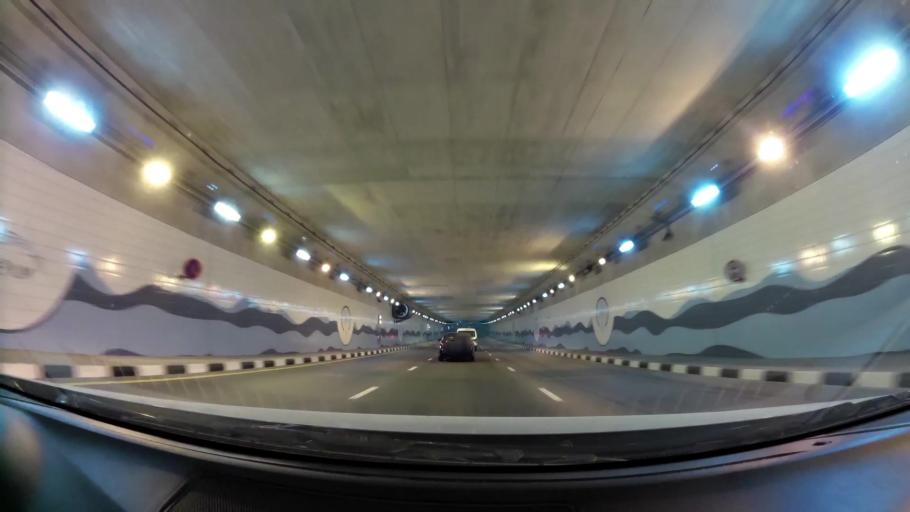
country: AE
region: Dubai
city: Dubai
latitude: 25.1251
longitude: 55.1165
